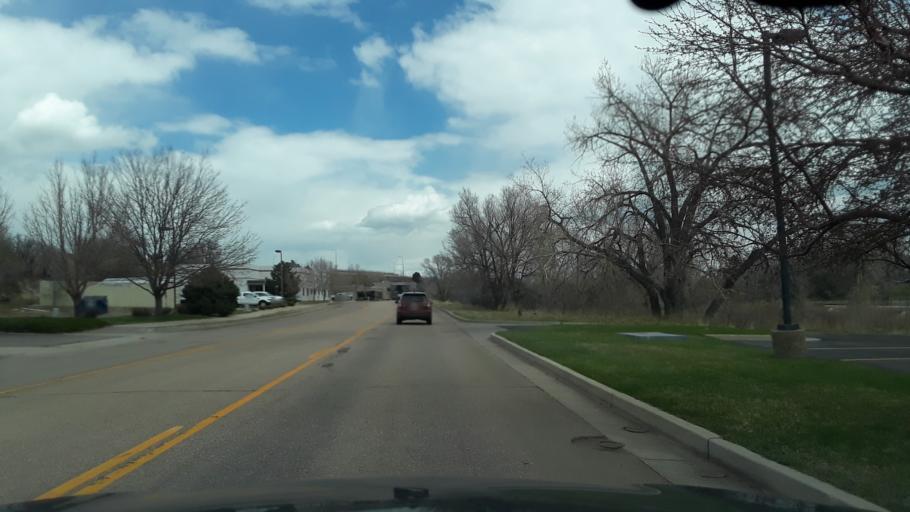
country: US
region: Colorado
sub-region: El Paso County
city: Colorado Springs
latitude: 38.9054
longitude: -104.8242
